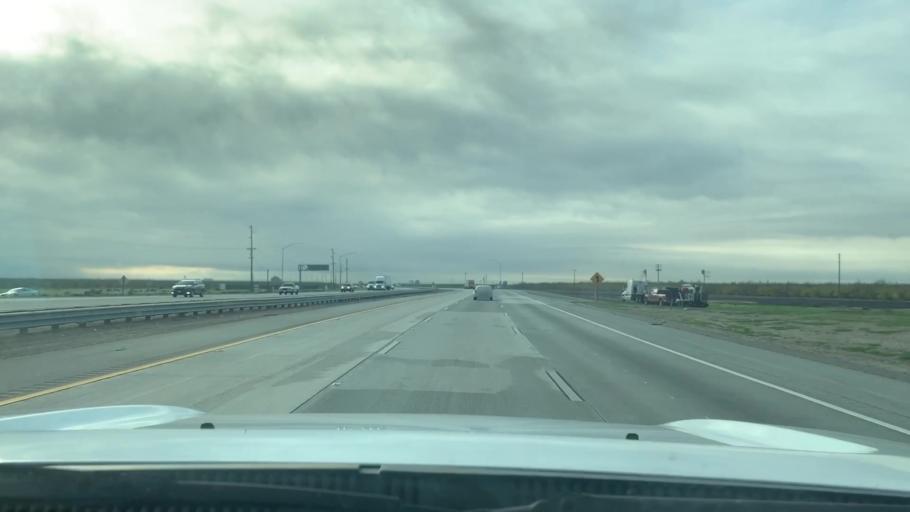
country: US
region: California
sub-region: Kern County
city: Shafter
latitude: 35.5283
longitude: -119.1896
